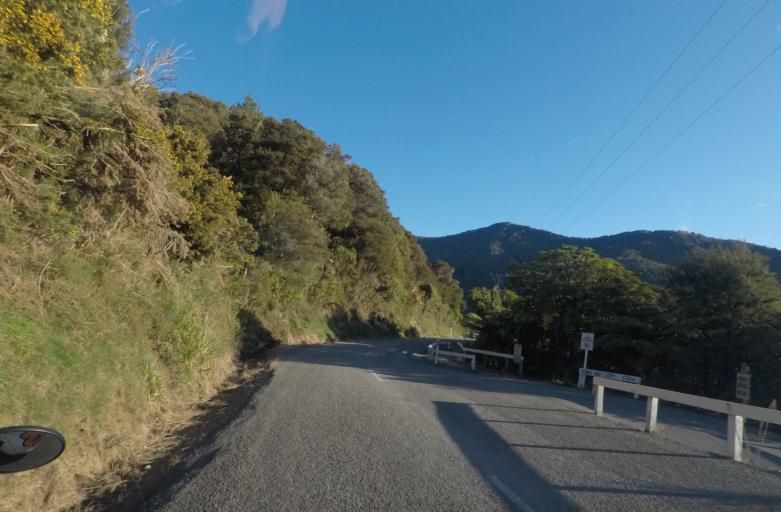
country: NZ
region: Marlborough
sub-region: Marlborough District
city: Picton
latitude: -41.2737
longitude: 173.9680
